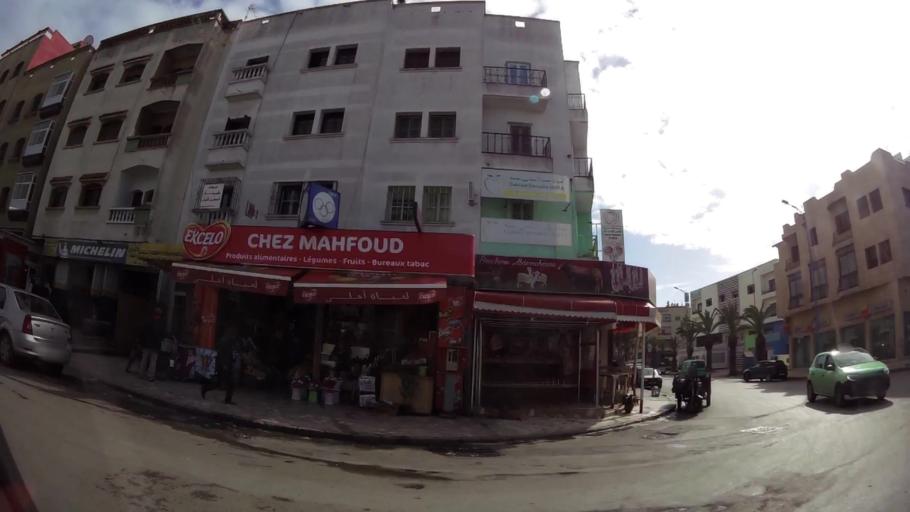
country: MA
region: Grand Casablanca
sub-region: Mohammedia
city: Mohammedia
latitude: 33.6941
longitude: -7.3787
